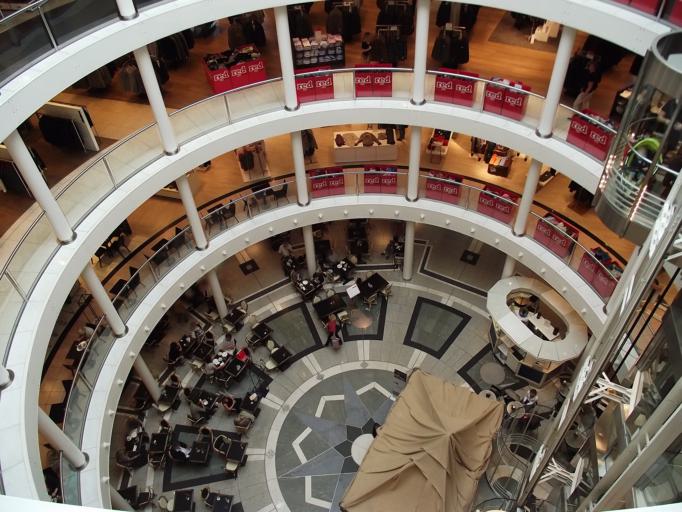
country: DE
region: Baden-Wuerttemberg
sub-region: Regierungsbezirk Stuttgart
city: Stuttgart
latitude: 48.7749
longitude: 9.1805
